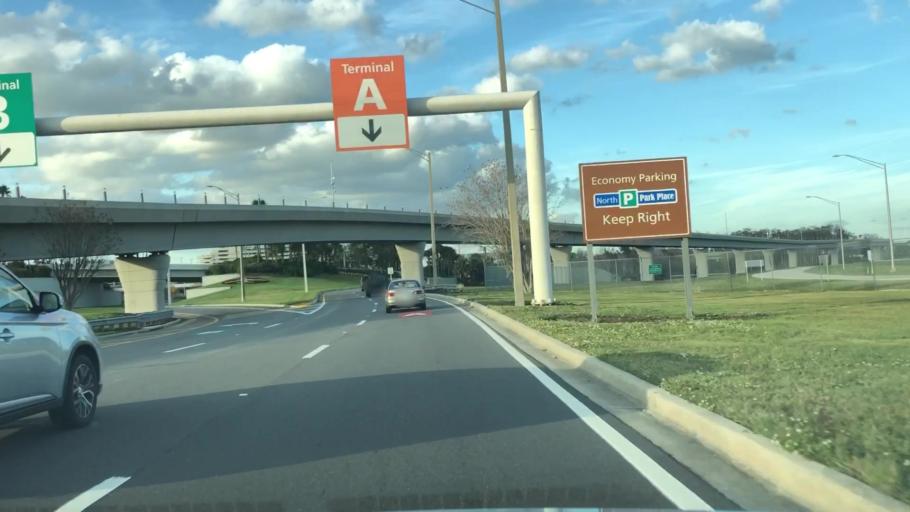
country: US
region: Florida
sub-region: Orange County
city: Taft
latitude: 28.4249
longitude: -81.3064
